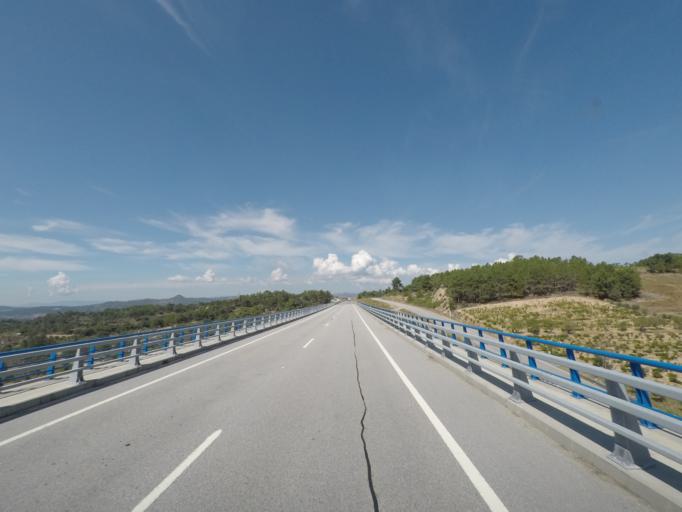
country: PT
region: Braganca
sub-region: Carrazeda de Ansiaes
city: Carrazeda de Anciaes
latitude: 41.2707
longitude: -7.3217
